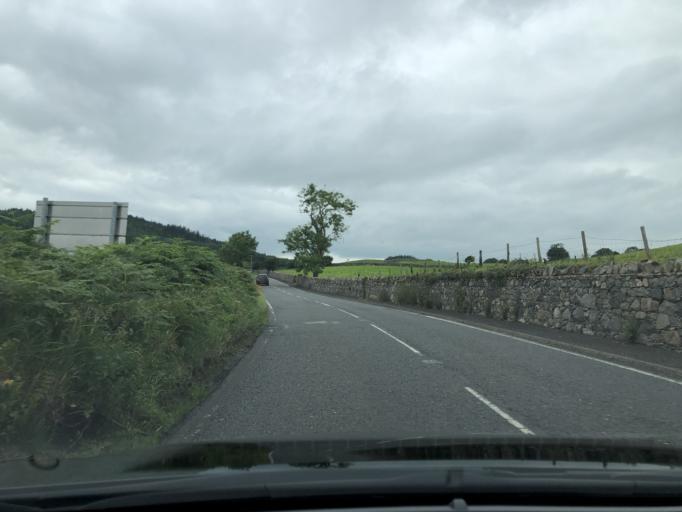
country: GB
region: Northern Ireland
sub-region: Down District
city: Castlewellan
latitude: 54.2568
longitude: -5.9648
